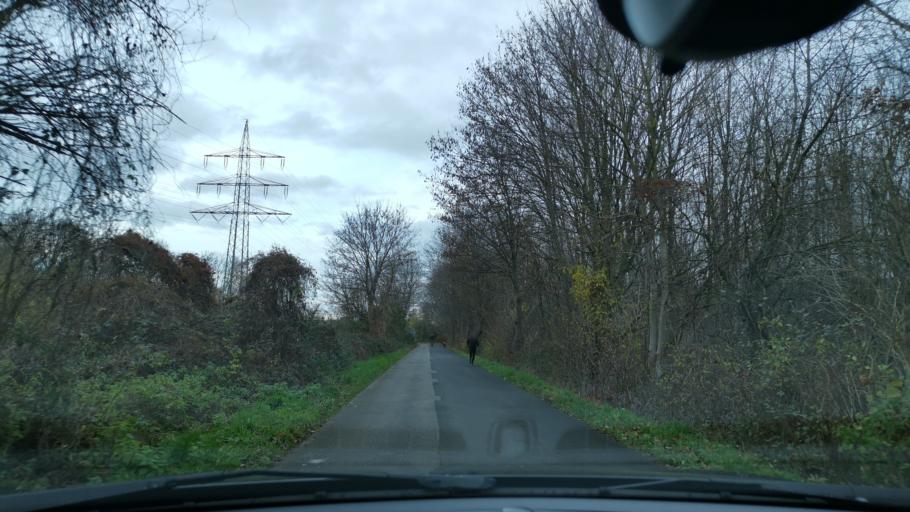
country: DE
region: North Rhine-Westphalia
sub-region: Regierungsbezirk Dusseldorf
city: Grevenbroich
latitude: 51.0581
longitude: 6.5715
